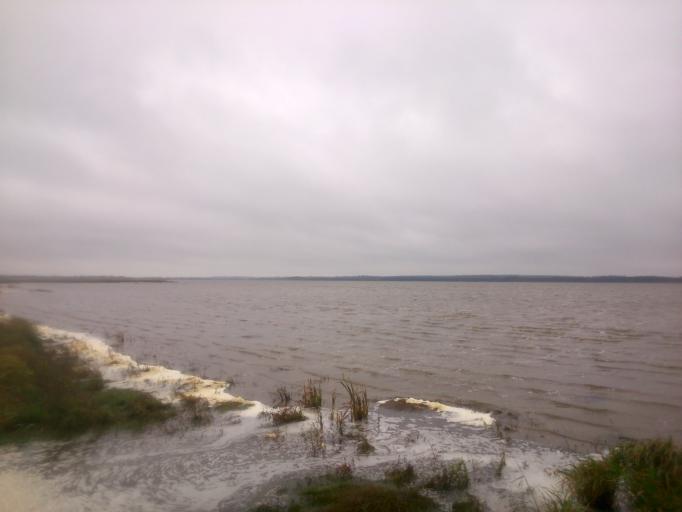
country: DK
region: South Denmark
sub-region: Varde Kommune
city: Oksbol
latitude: 55.6980
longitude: 8.2169
